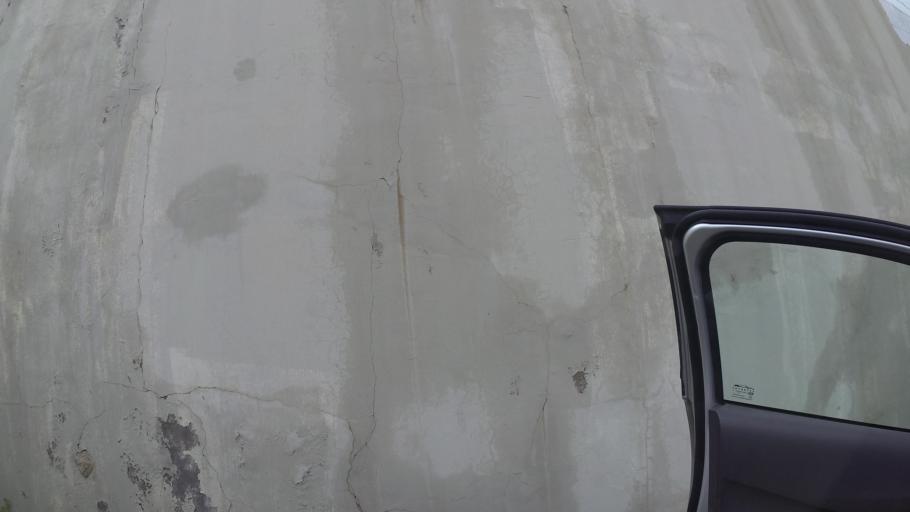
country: JO
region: Amman
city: Al Jubayhah
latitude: 32.0242
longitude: 35.8266
